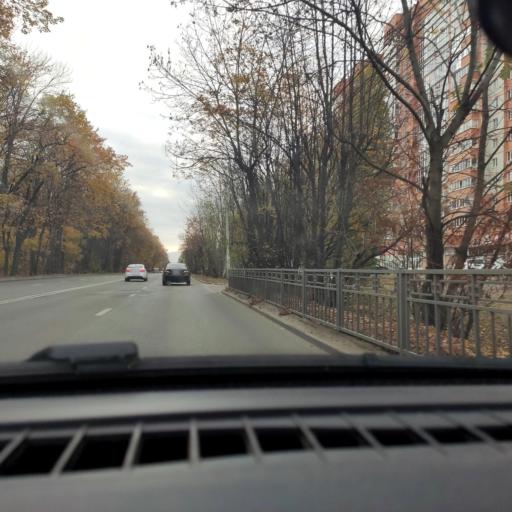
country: RU
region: Voronezj
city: Voronezh
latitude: 51.7264
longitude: 39.2111
